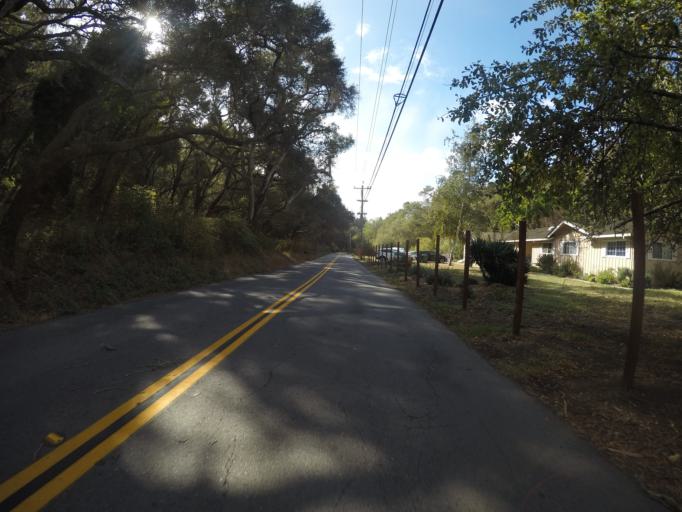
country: US
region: California
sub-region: Santa Cruz County
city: Soquel
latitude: 37.0096
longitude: -121.9650
